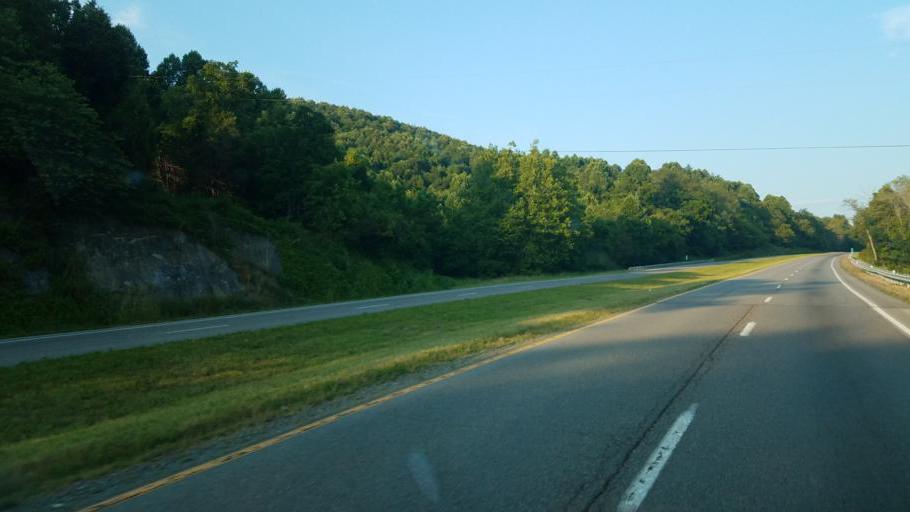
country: US
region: Tennessee
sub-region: Hawkins County
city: Mount Carmel
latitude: 36.6417
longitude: -82.7020
